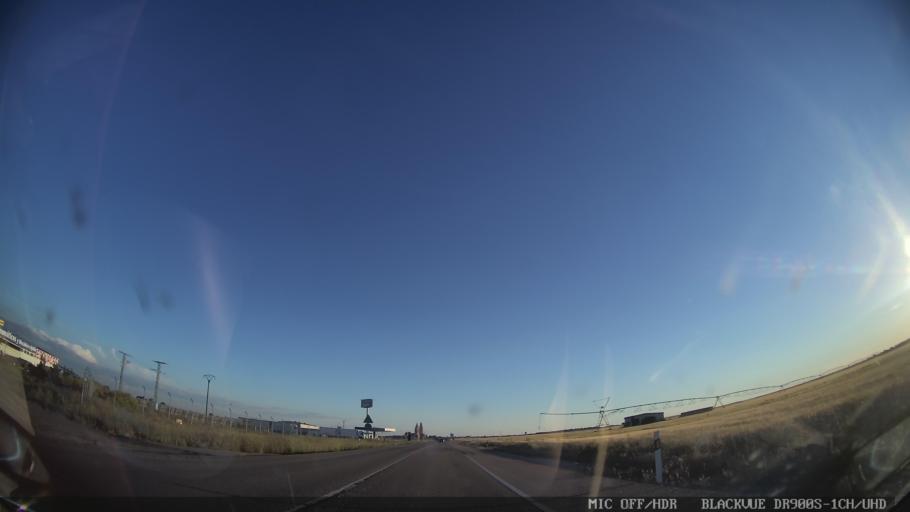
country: ES
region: Castille and Leon
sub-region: Provincia de Valladolid
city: Alaejos
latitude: 41.3205
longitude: -5.2042
